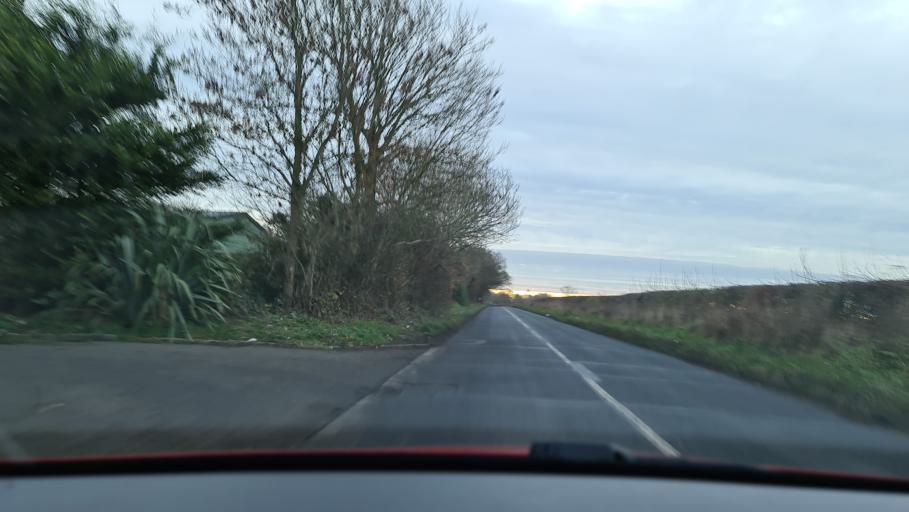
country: GB
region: England
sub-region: Buckinghamshire
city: Amersham
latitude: 51.6897
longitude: -0.6308
